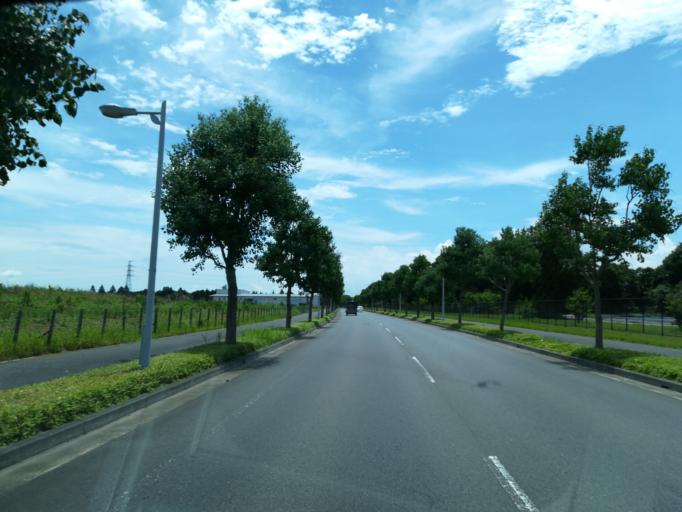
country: JP
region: Ibaraki
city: Naka
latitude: 36.0780
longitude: 140.0792
